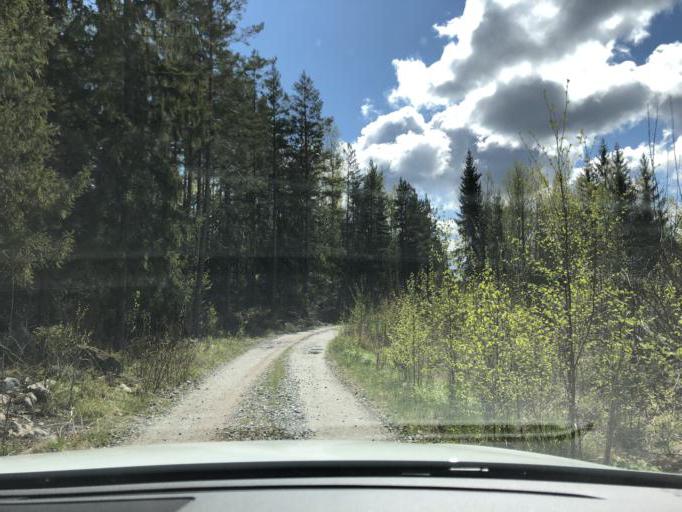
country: SE
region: Uppsala
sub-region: Heby Kommun
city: Tarnsjo
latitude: 60.2409
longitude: 16.7043
